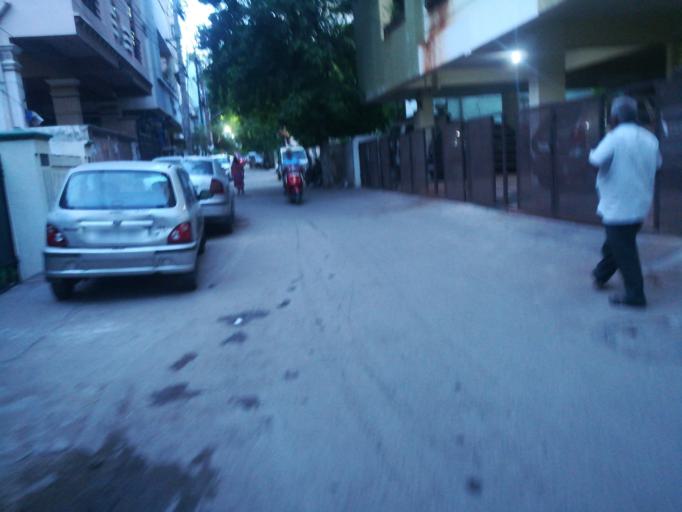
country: IN
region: Telangana
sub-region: Hyderabad
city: Malkajgiri
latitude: 17.4217
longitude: 78.5159
